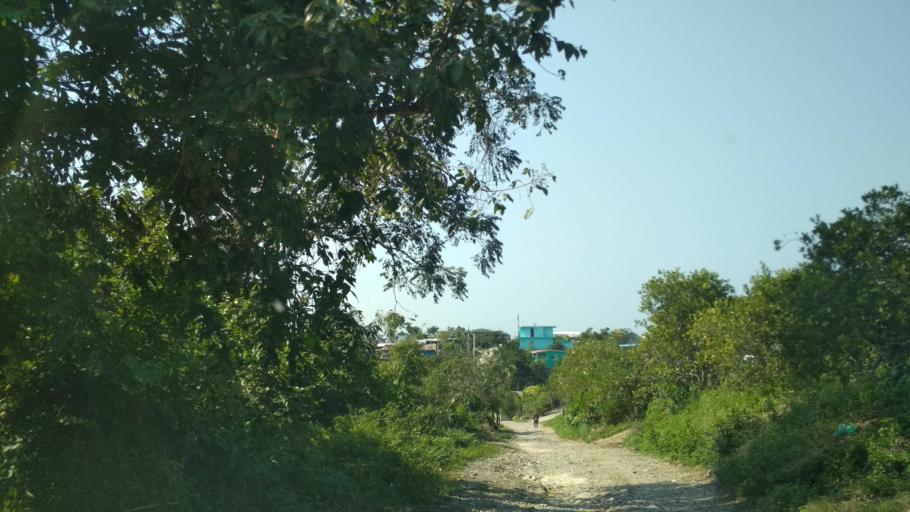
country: MX
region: Veracruz
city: Agua Dulce
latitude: 20.3851
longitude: -97.2119
